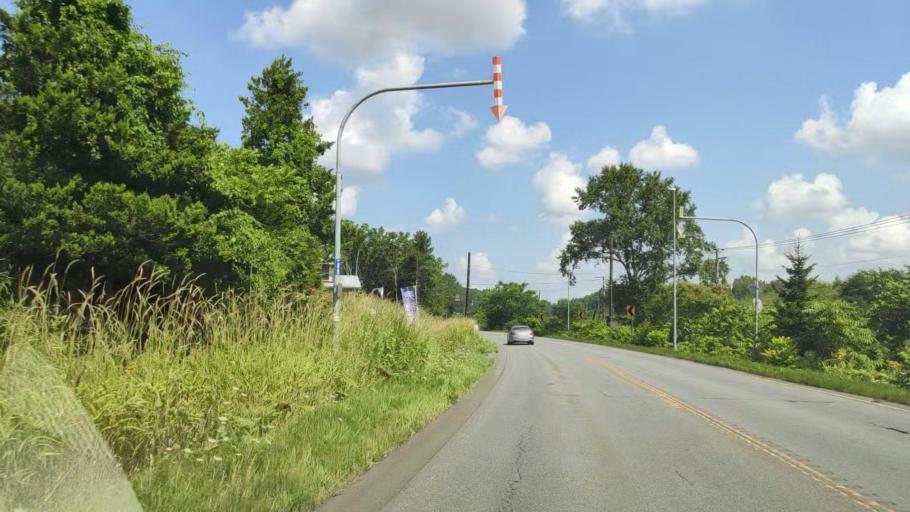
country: JP
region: Hokkaido
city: Shimo-furano
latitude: 43.5605
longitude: 142.4353
